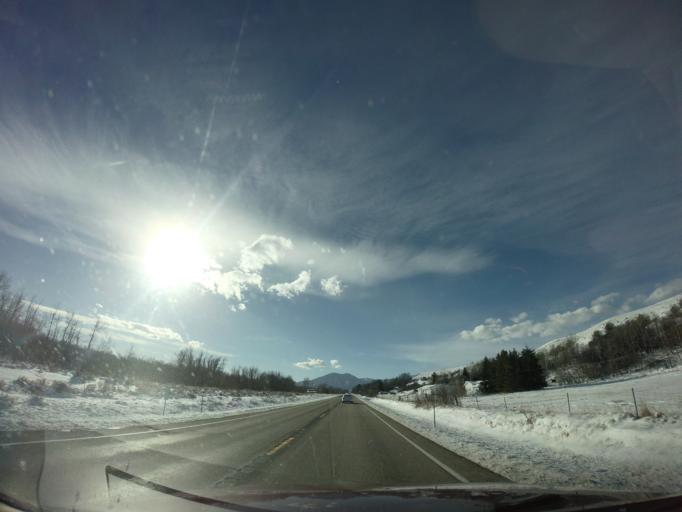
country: US
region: Montana
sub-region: Carbon County
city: Red Lodge
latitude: 45.2336
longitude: -109.2378
